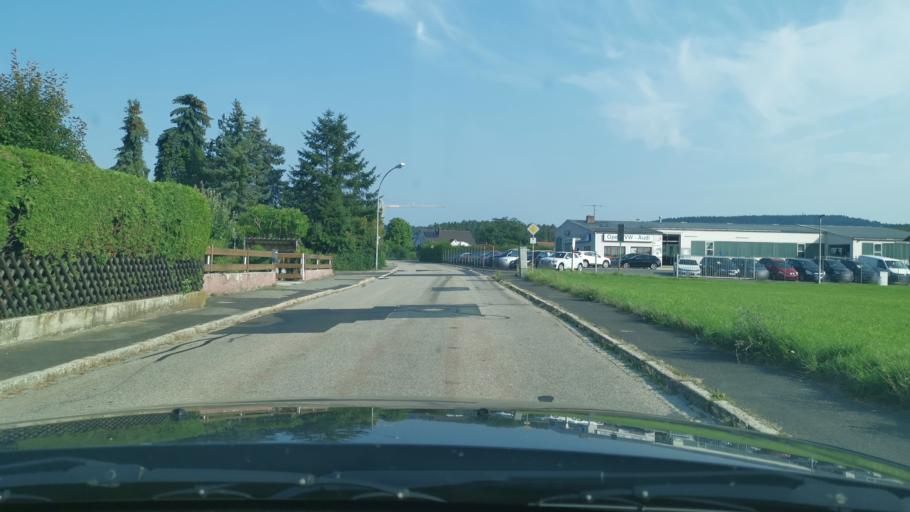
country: DE
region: Bavaria
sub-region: Upper Palatinate
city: Schnaittenbach
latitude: 49.5531
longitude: 12.0046
